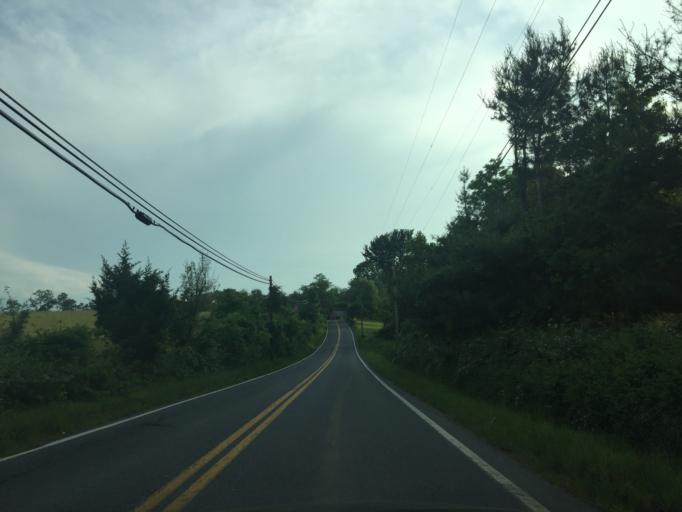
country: US
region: Maryland
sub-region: Frederick County
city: Point of Rocks
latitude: 39.2886
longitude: -77.5255
